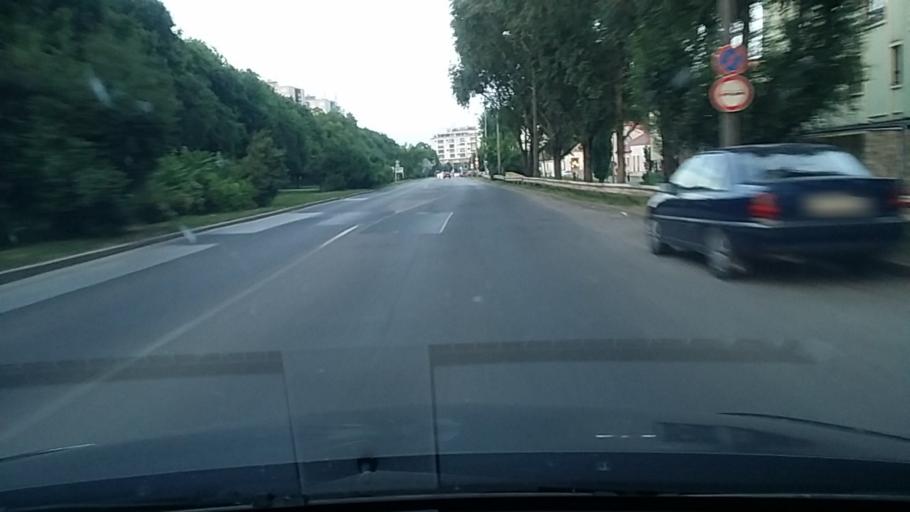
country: HU
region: Borsod-Abauj-Zemplen
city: Miskolc
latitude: 48.1070
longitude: 20.7802
